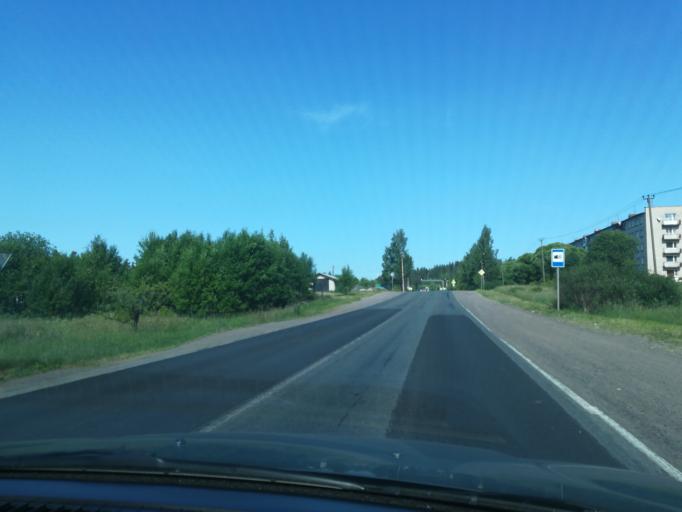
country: RU
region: Leningrad
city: Lesogorskiy
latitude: 61.0870
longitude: 28.9058
